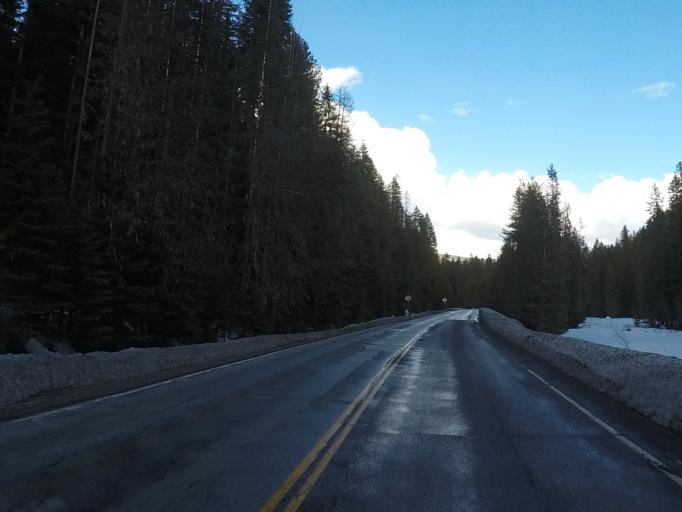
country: US
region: Montana
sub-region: Ravalli County
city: Hamilton
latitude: 46.5158
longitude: -114.7138
